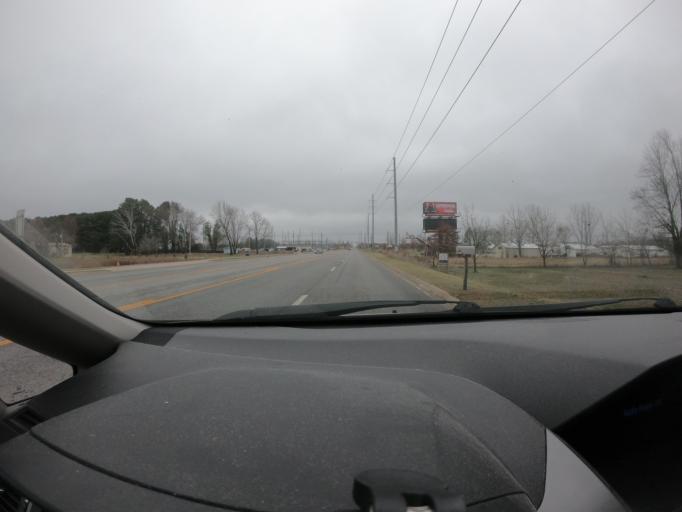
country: US
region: Arkansas
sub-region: Benton County
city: Centerton
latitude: 36.3578
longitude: -94.2519
